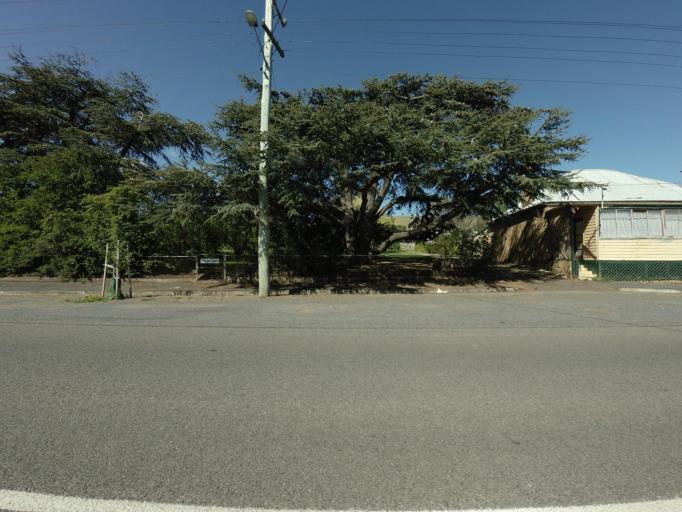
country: AU
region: Tasmania
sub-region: Derwent Valley
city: New Norfolk
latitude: -42.5557
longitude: 146.8344
